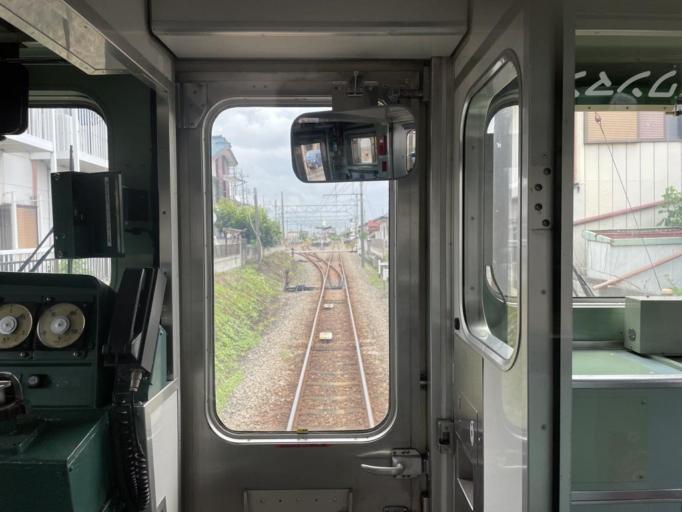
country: JP
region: Gunma
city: Yoshii
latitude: 36.2559
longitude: 138.9825
